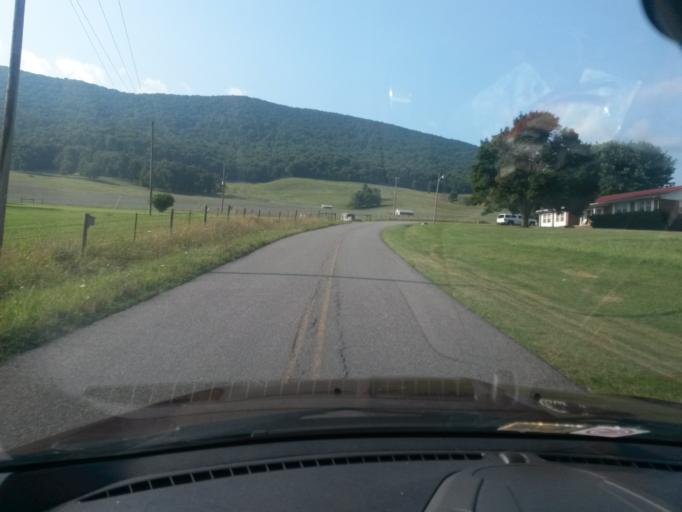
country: US
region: Virginia
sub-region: Giles County
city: Narrows
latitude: 37.3780
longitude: -80.7936
